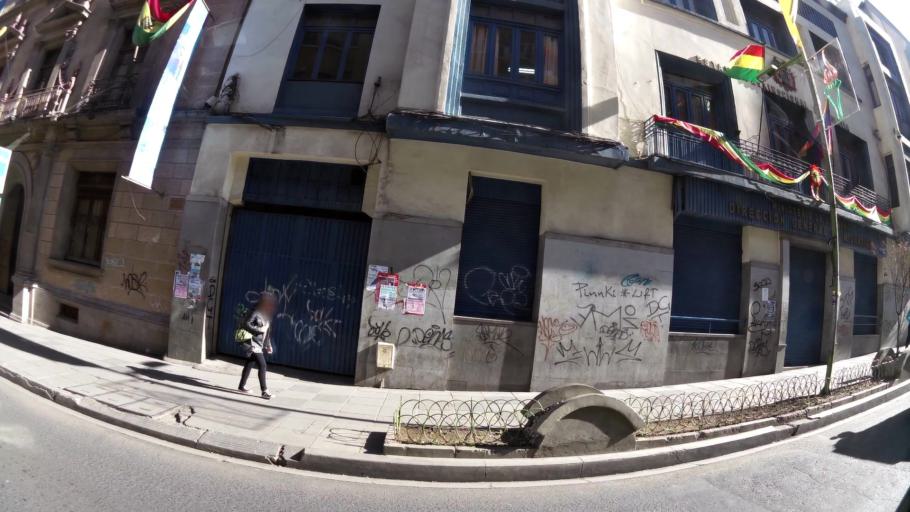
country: BO
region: La Paz
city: La Paz
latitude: -16.4998
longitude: -68.1324
